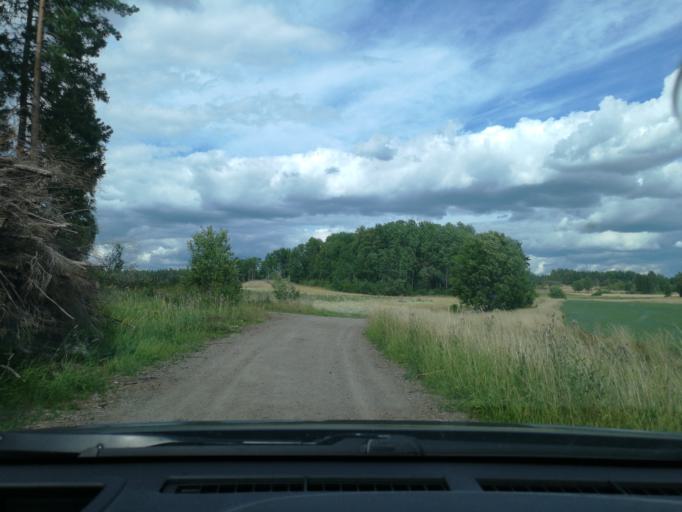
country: SE
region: Stockholm
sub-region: Sigtuna Kommun
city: Marsta
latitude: 59.6125
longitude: 17.8002
